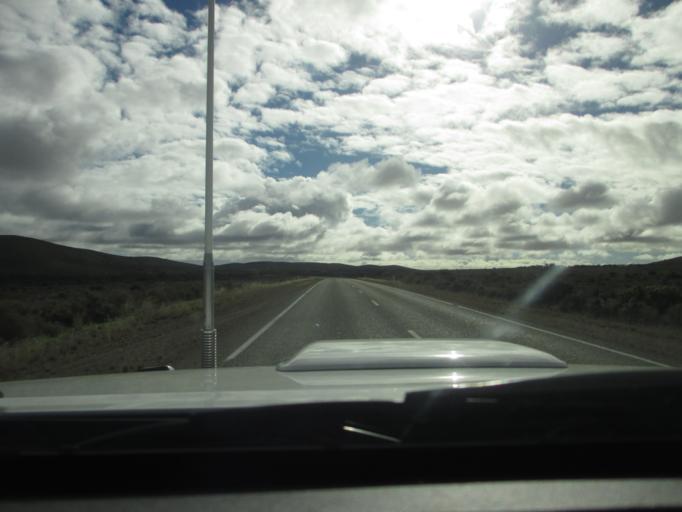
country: AU
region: South Australia
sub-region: Flinders Ranges
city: Quorn
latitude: -32.2204
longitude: 138.5185
